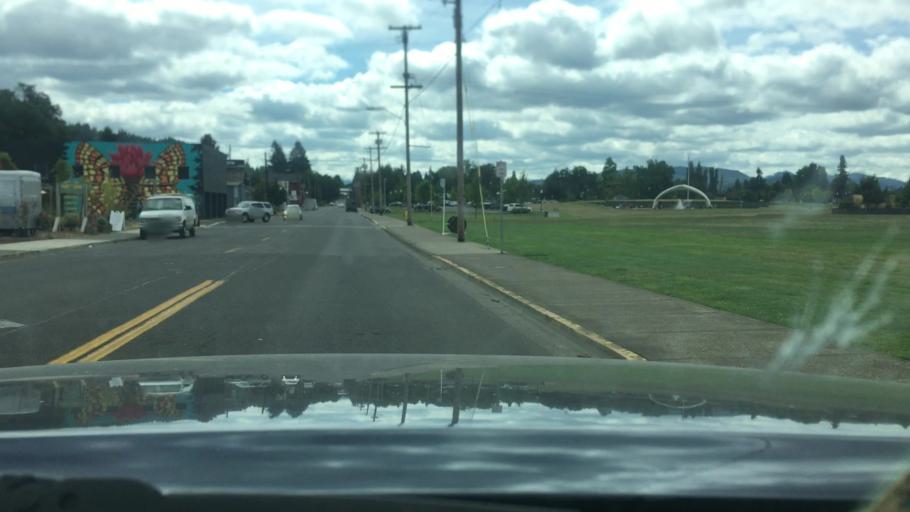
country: US
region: Oregon
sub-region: Lane County
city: Cottage Grove
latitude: 43.7970
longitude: -123.0580
